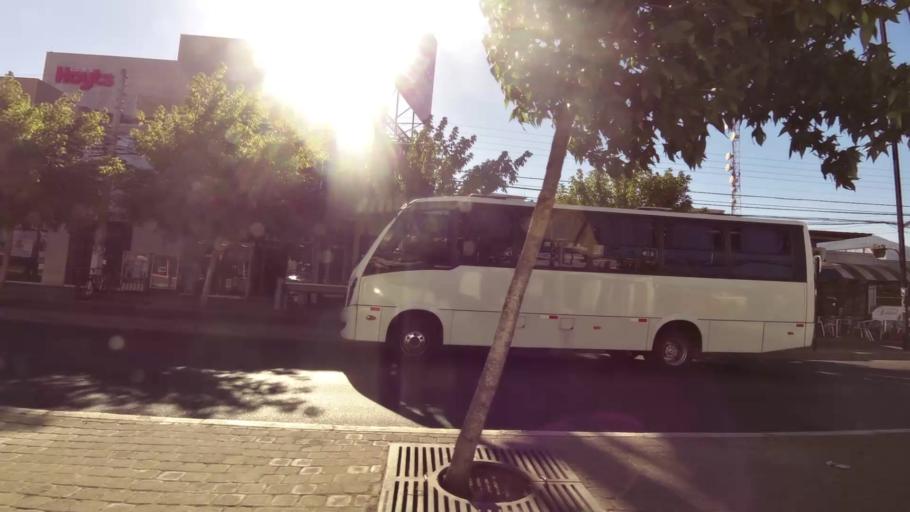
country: CL
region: O'Higgins
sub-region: Provincia de Colchagua
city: Chimbarongo
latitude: -34.5860
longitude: -70.9846
